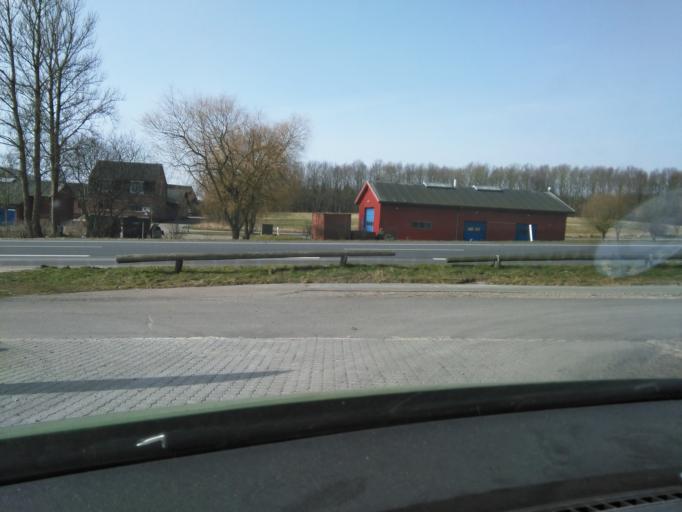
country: DK
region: Central Jutland
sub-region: Arhus Kommune
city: Beder
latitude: 56.0830
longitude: 10.2100
